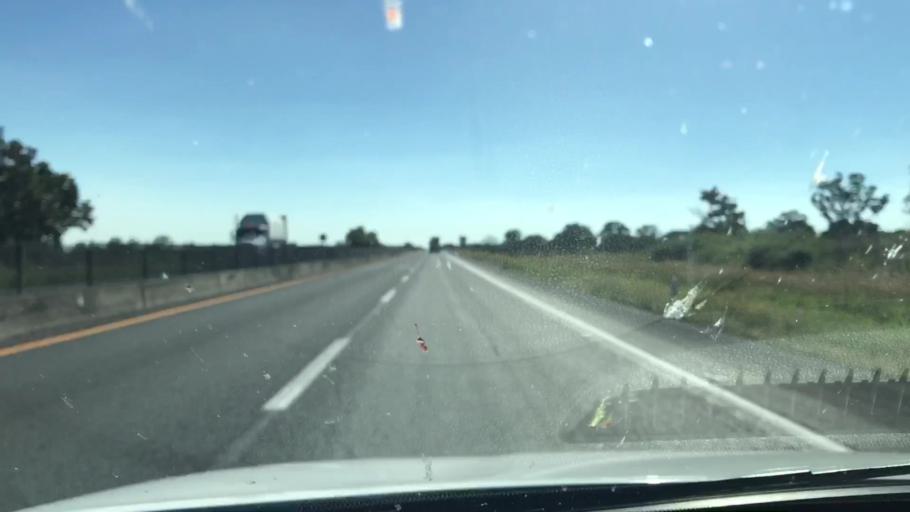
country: MX
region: Jalisco
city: Tepatitlan de Morelos
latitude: 20.8647
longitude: -102.7595
